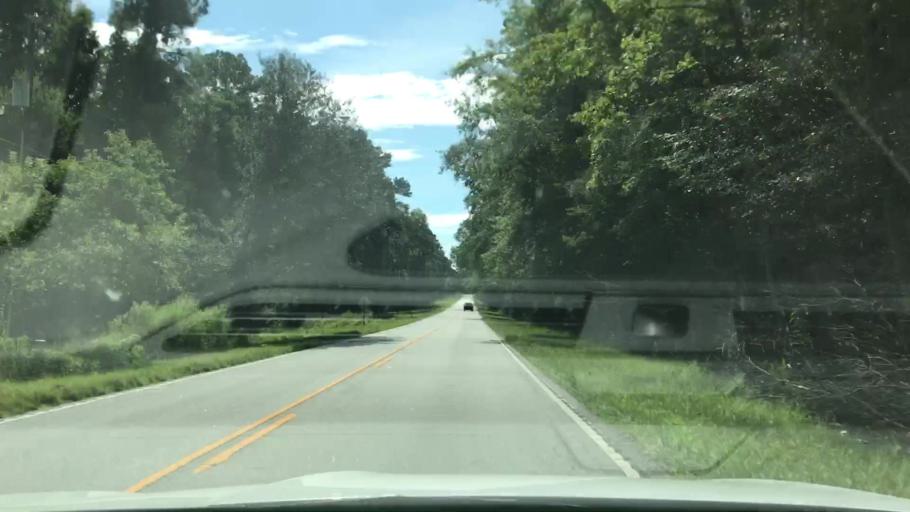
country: US
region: South Carolina
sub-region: Dorchester County
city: Centerville
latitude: 32.9445
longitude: -80.1945
